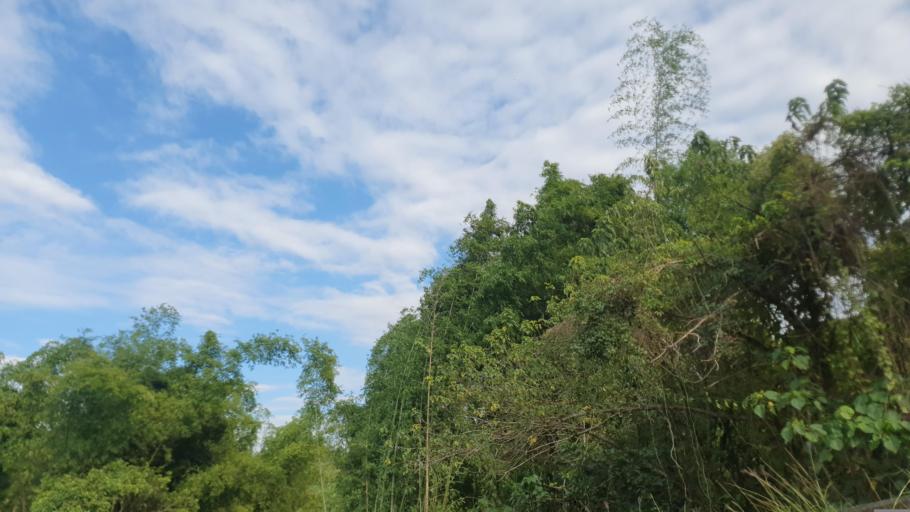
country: TW
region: Taiwan
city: Yujing
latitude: 23.0196
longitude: 120.4147
